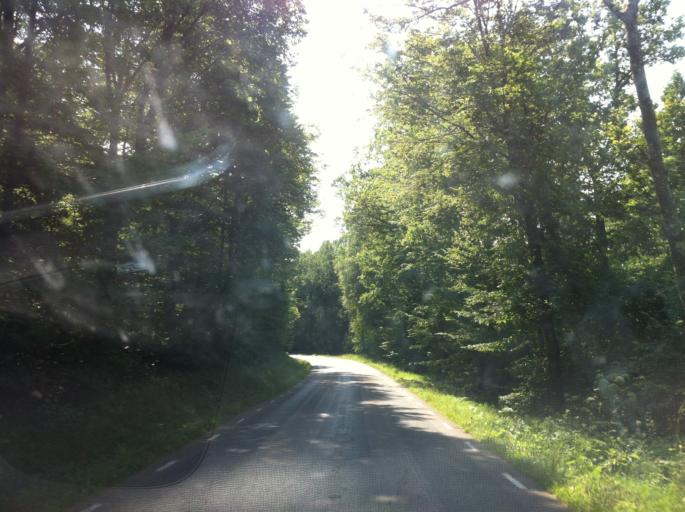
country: SE
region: Skane
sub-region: Hoors Kommun
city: Hoeoer
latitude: 56.0110
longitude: 13.4927
